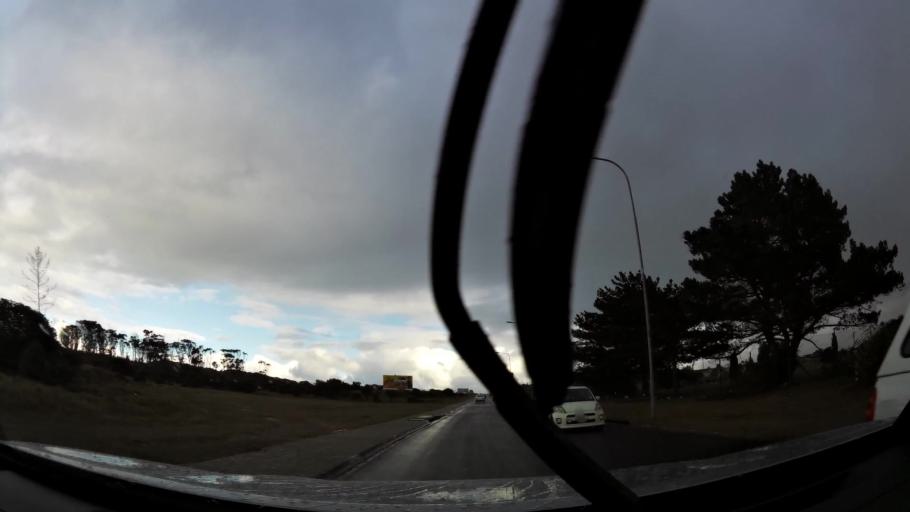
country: ZA
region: Western Cape
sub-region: Eden District Municipality
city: Mossel Bay
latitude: -34.1855
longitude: 22.0929
